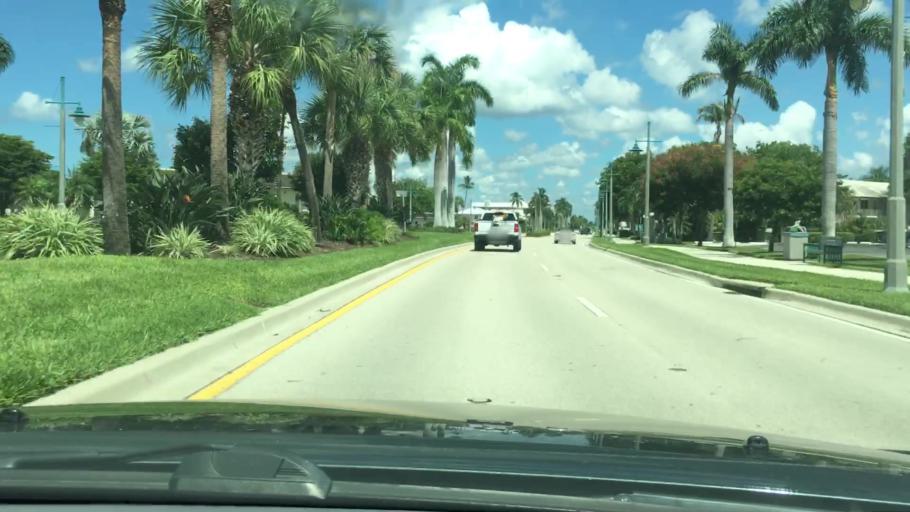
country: US
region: Florida
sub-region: Collier County
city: Marco
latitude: 25.9385
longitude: -81.7325
